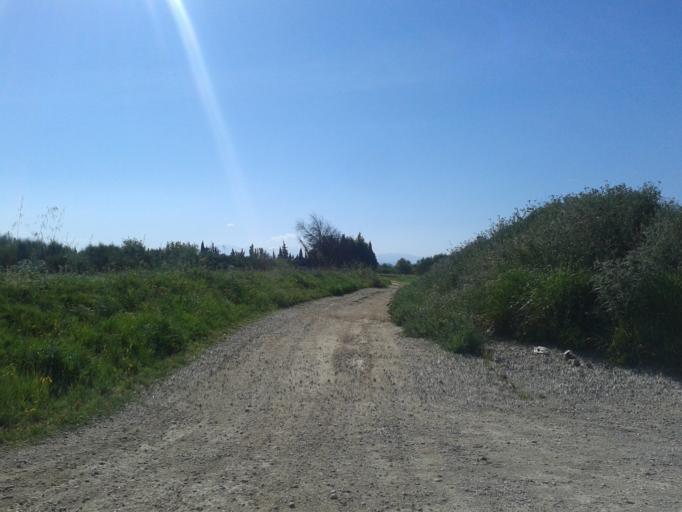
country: FR
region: Languedoc-Roussillon
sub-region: Departement des Pyrenees-Orientales
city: Pezilla-la-Riviere
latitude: 42.7003
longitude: 2.7529
